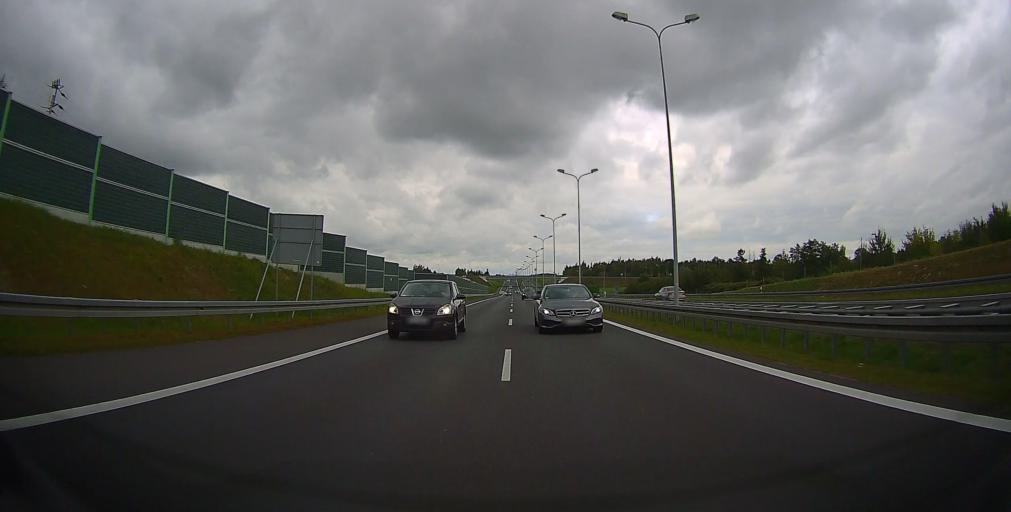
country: PL
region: Masovian Voivodeship
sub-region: Powiat grojecki
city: Goszczyn
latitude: 51.7660
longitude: 20.8601
